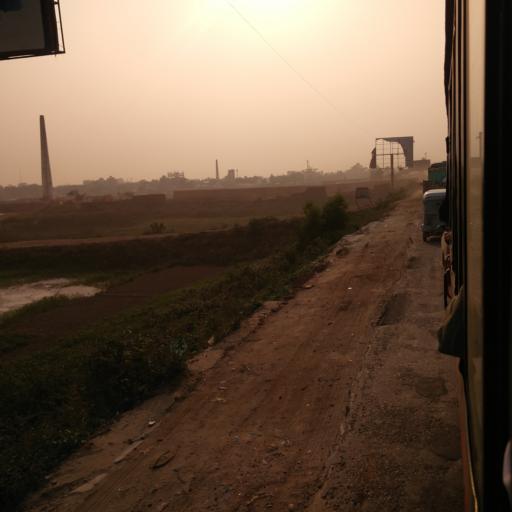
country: BD
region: Dhaka
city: Tungi
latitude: 23.8959
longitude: 90.3401
